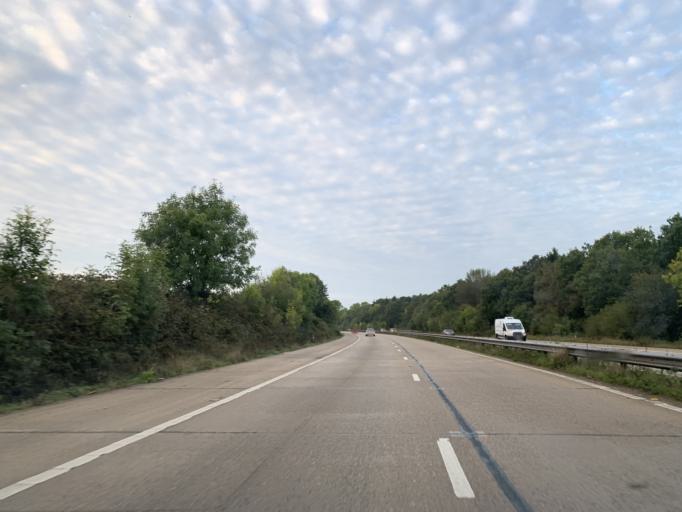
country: GB
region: England
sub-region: Hampshire
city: Totton
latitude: 50.9538
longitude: -1.4737
